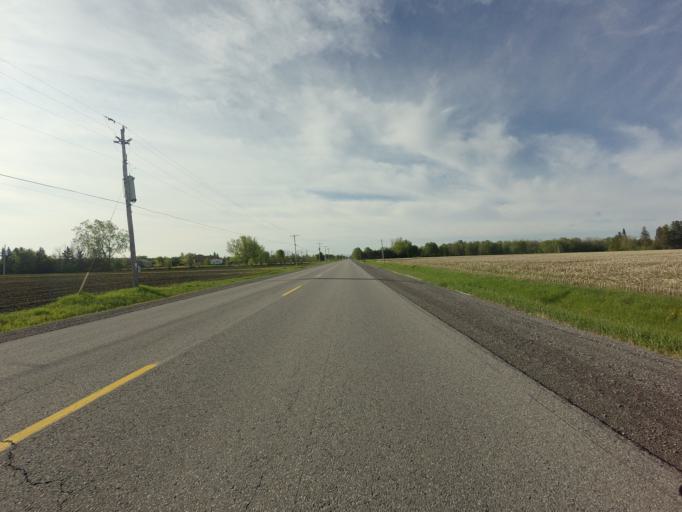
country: CA
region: Ontario
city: Ottawa
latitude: 45.2882
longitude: -75.4472
